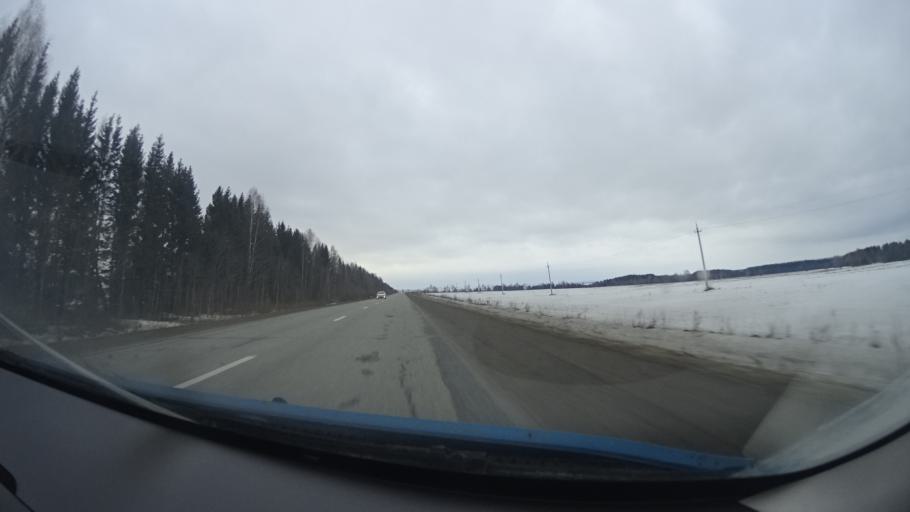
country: RU
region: Perm
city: Osa
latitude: 57.3480
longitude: 55.5933
